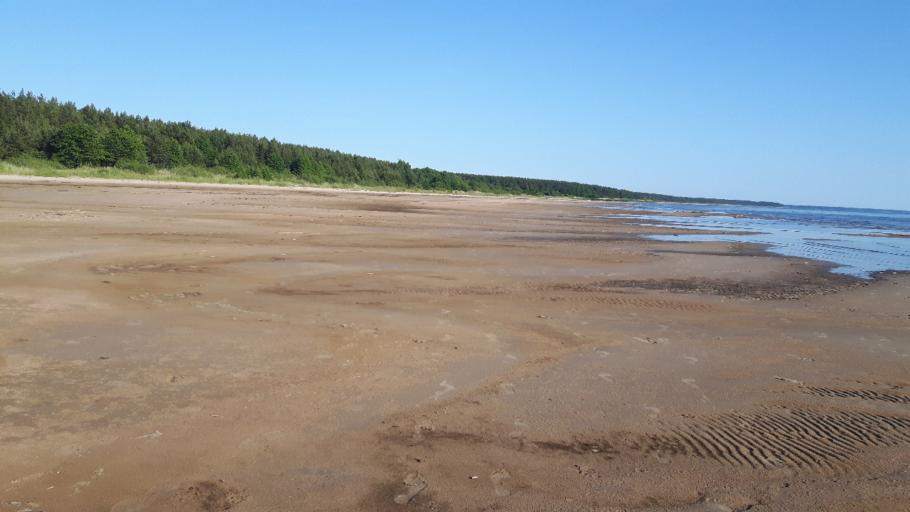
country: LV
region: Salacgrivas
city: Salacgriva
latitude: 57.6922
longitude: 24.3525
